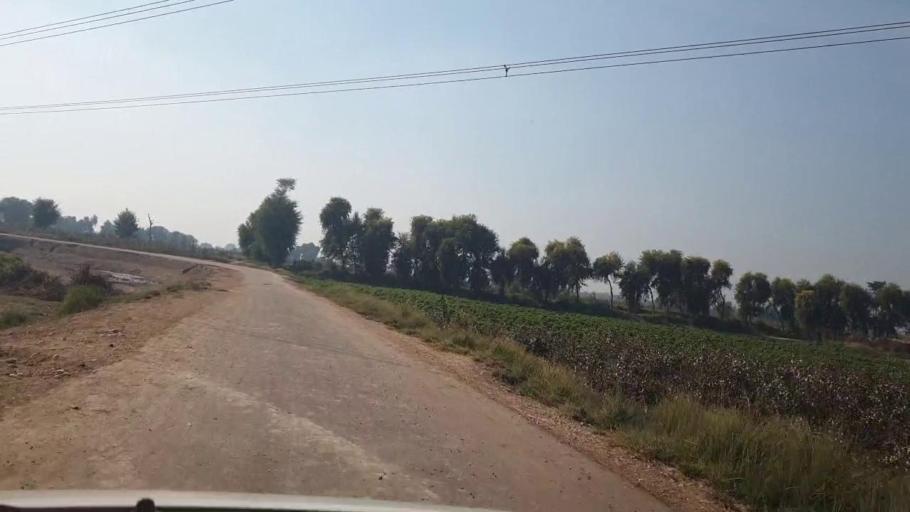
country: PK
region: Sindh
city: Bhan
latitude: 26.6064
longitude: 67.7541
